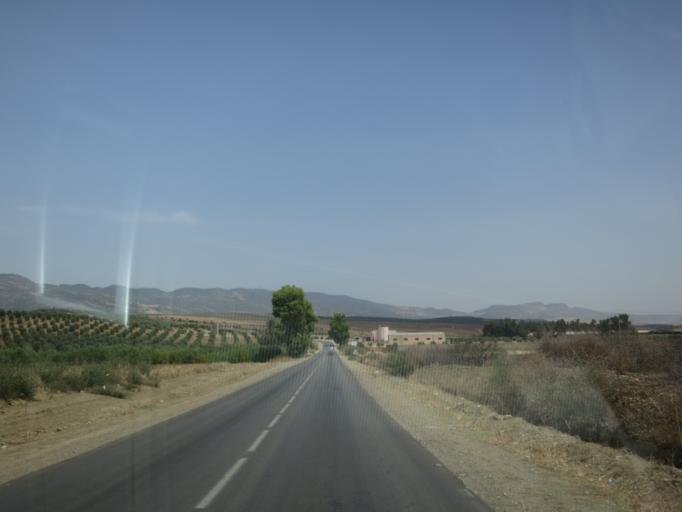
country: MA
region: Meknes-Tafilalet
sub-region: Meknes
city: Meknes
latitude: 33.9796
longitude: -5.5674
